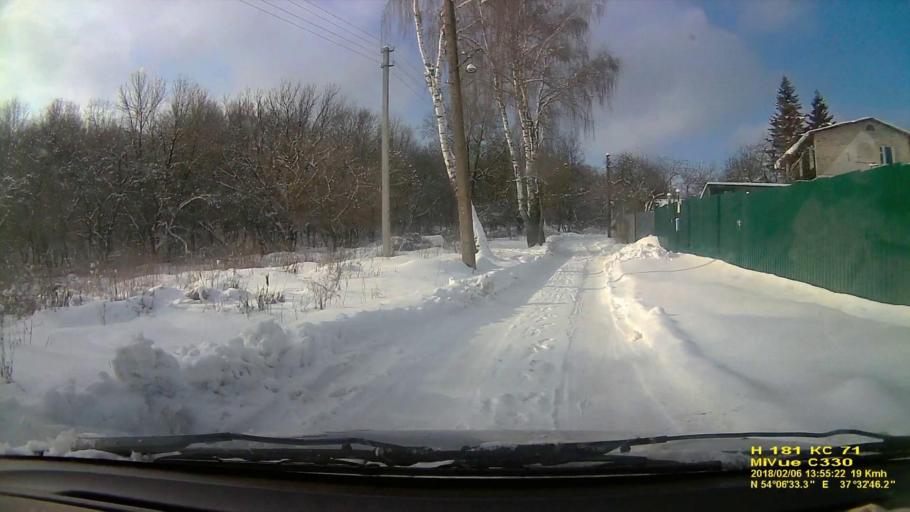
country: RU
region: Tula
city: Kosaya Gora
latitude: 54.1093
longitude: 37.5459
